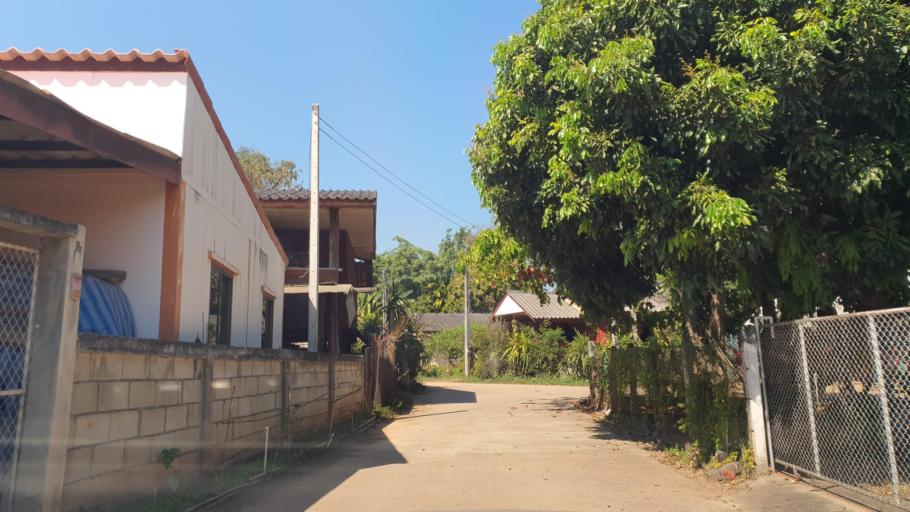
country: TH
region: Lampang
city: Wang Nuea
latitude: 19.1853
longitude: 99.5032
